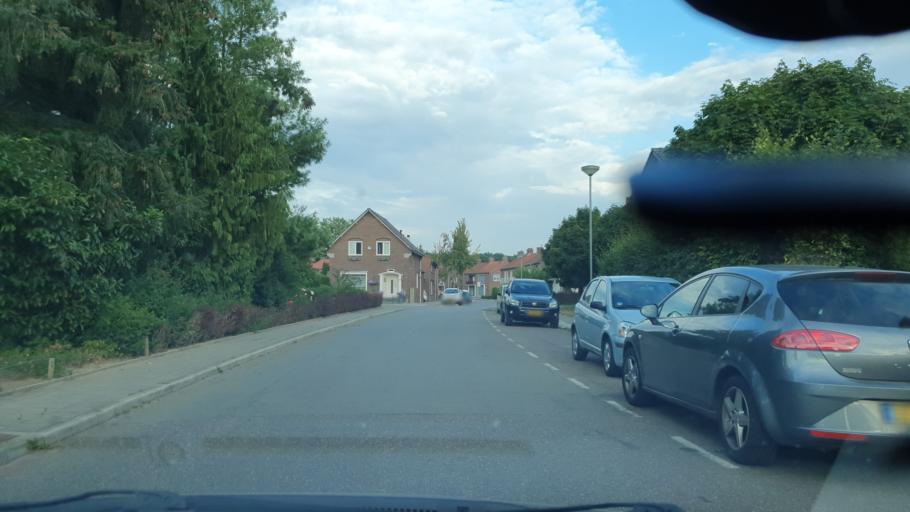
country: NL
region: Limburg
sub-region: Gemeente Roerdalen
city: Sint Odilienberg
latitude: 51.1452
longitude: 6.0010
